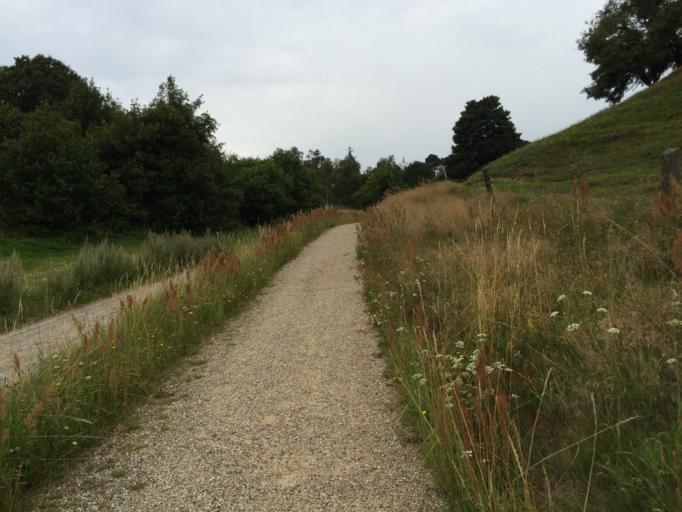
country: DK
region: Central Jutland
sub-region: Syddjurs Kommune
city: Ronde
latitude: 56.2273
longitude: 10.5373
